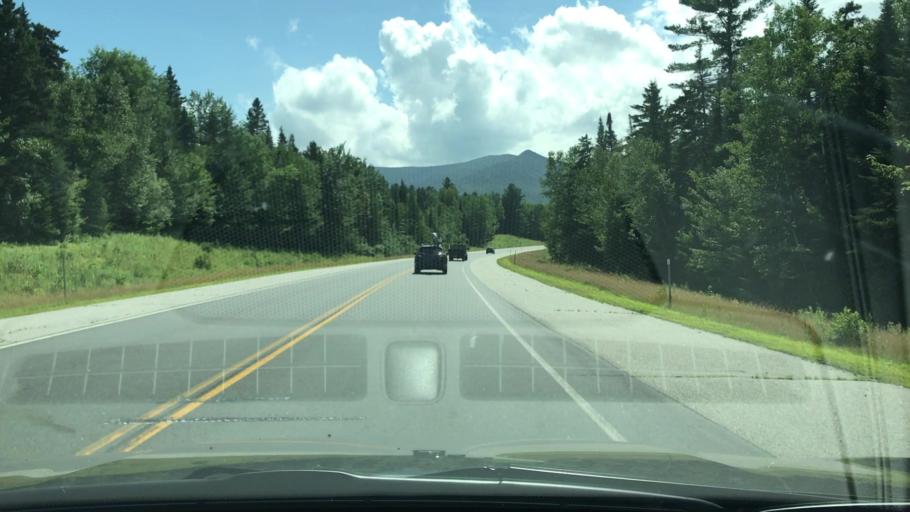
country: US
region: New Hampshire
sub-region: Coos County
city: Jefferson
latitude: 44.3704
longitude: -71.4438
